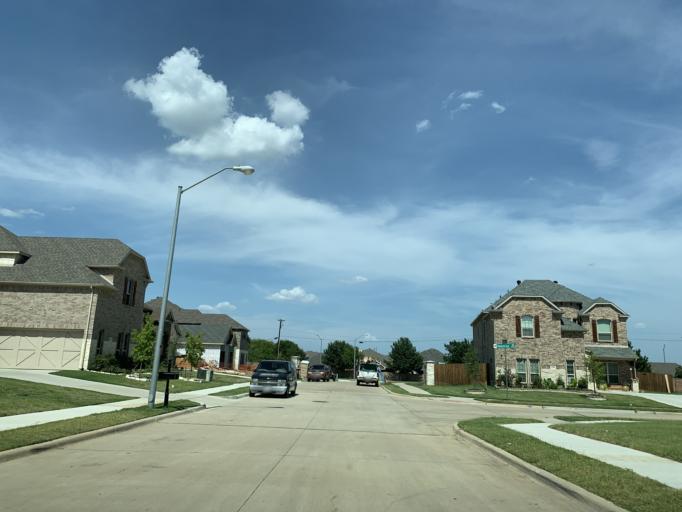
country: US
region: Texas
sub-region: Dallas County
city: Cedar Hill
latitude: 32.6472
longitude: -97.0081
